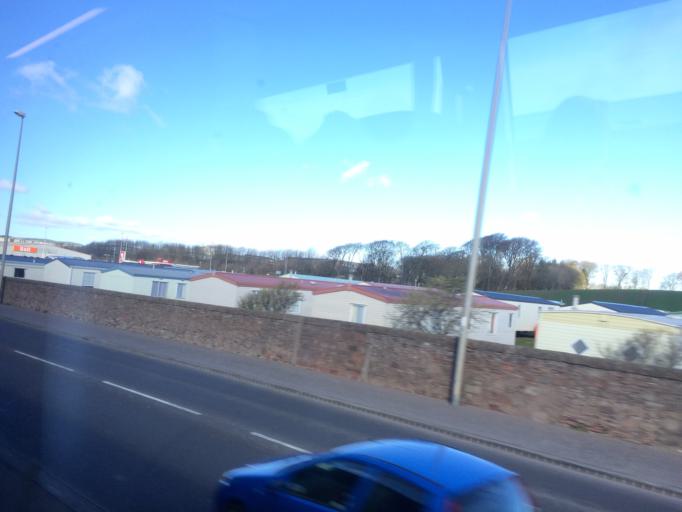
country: GB
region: Scotland
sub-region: Angus
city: Arbroath
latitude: 56.5506
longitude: -2.6082
